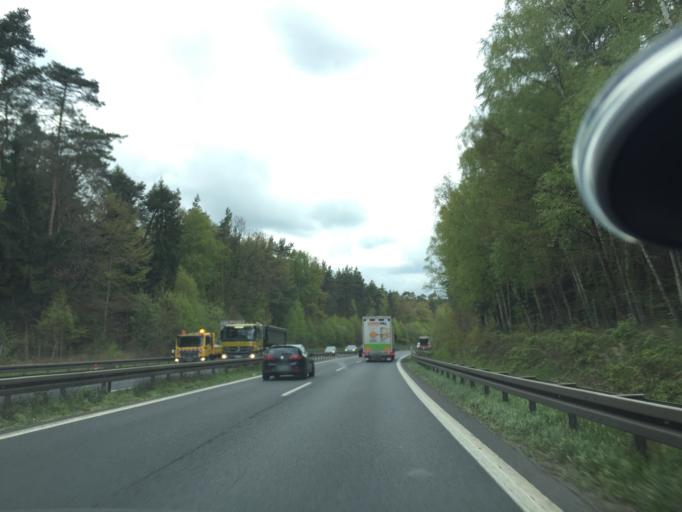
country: DE
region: Bavaria
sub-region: Regierungsbezirk Unterfranken
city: Stockstadt am Main
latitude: 49.9698
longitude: 9.0460
